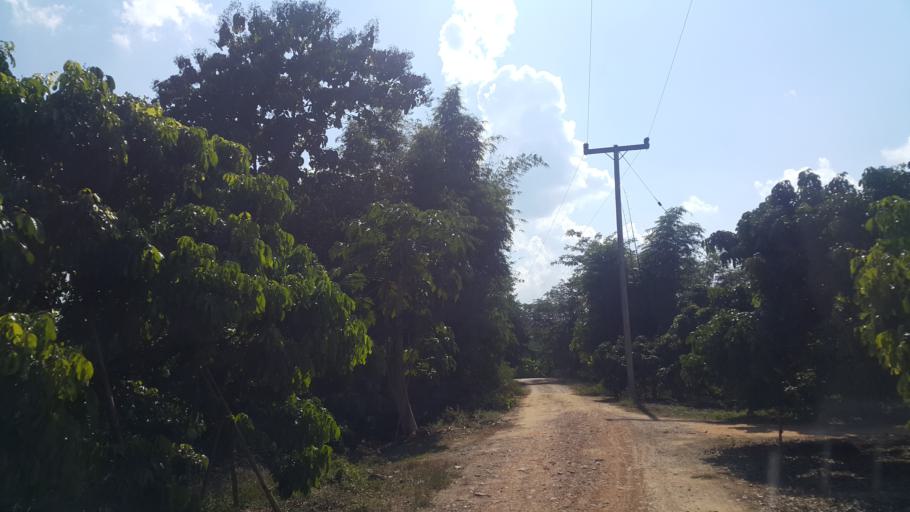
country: TH
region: Lamphun
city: Ban Thi
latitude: 18.6278
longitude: 99.1543
